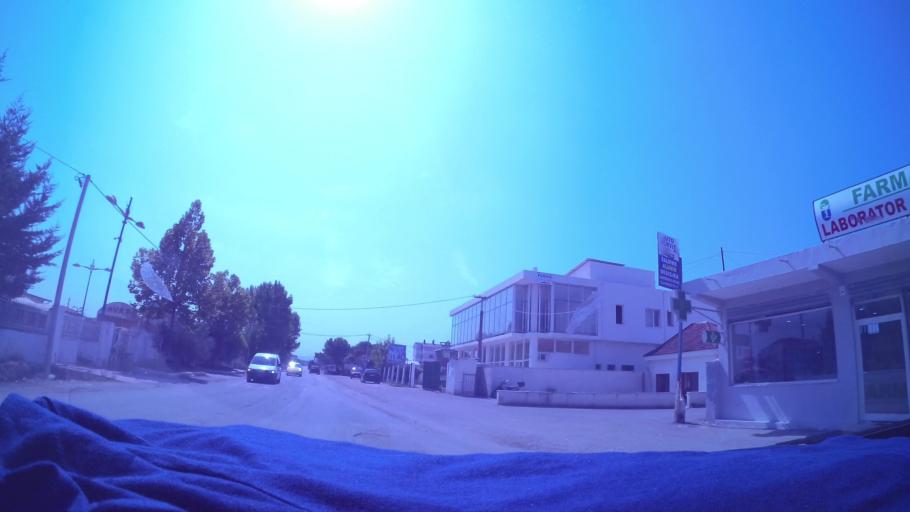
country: AL
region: Durres
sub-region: Rrethi i Durresit
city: Xhafzotaj
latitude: 41.3547
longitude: 19.5454
